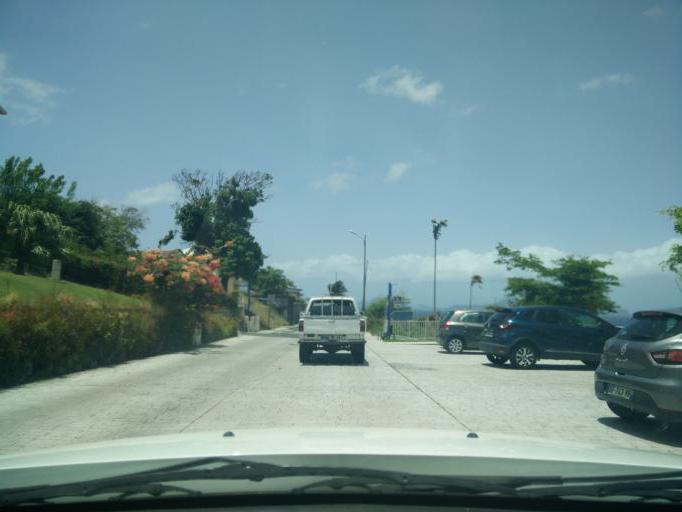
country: GP
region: Guadeloupe
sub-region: Guadeloupe
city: Gourbeyre
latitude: 15.9483
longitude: -61.6979
